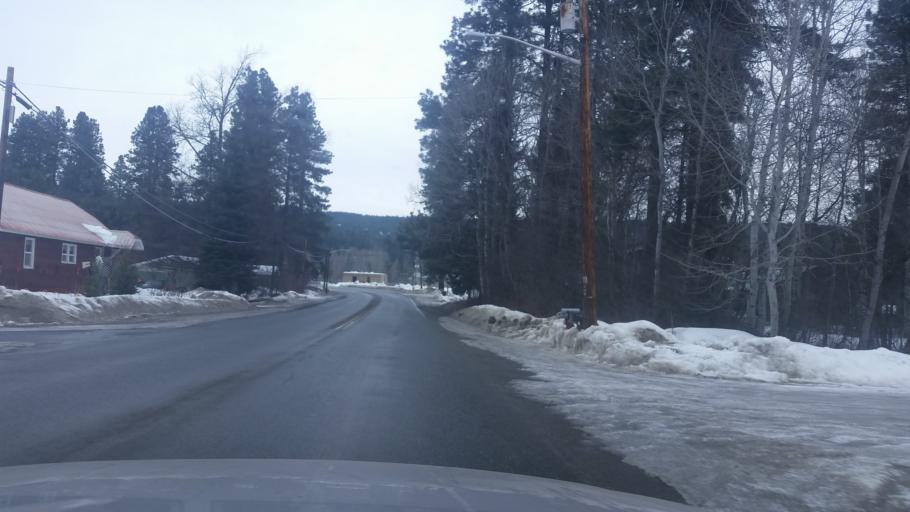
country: US
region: Washington
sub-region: Kittitas County
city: Cle Elum
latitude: 47.1888
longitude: -120.9481
